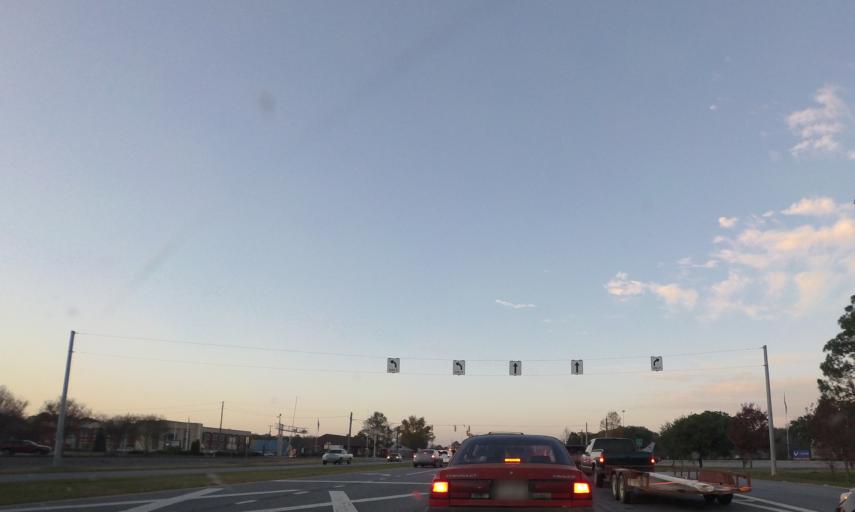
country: US
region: Georgia
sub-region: Houston County
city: Warner Robins
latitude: 32.6189
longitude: -83.5992
